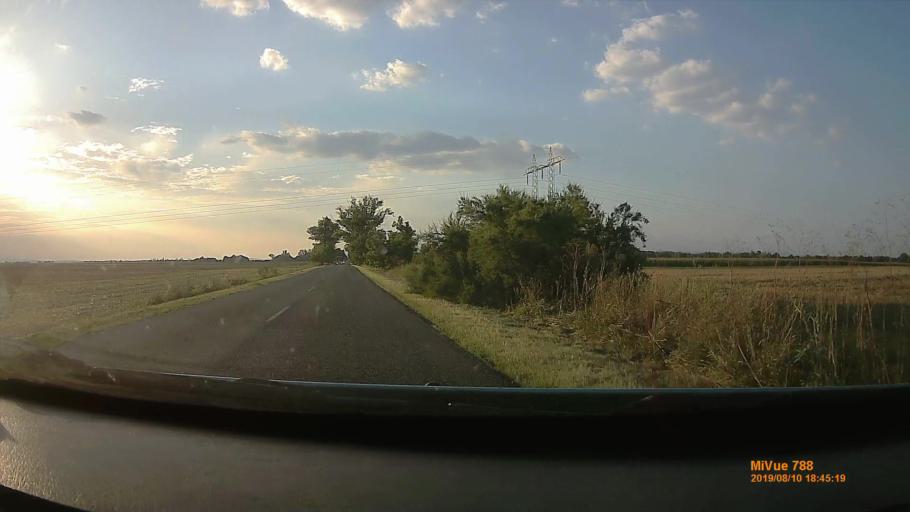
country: HU
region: Borsod-Abauj-Zemplen
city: Mezokovesd
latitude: 47.7638
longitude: 20.5995
